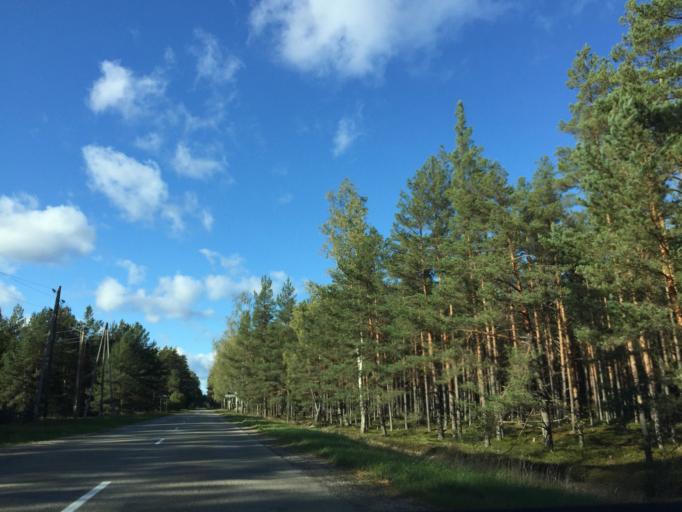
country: LV
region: Rojas
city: Roja
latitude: 57.4032
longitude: 22.9624
